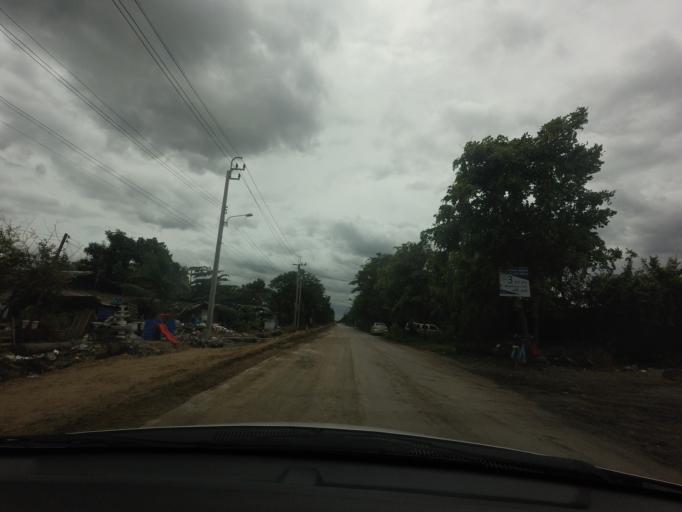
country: TH
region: Bangkok
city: Min Buri
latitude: 13.7826
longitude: 100.7613
